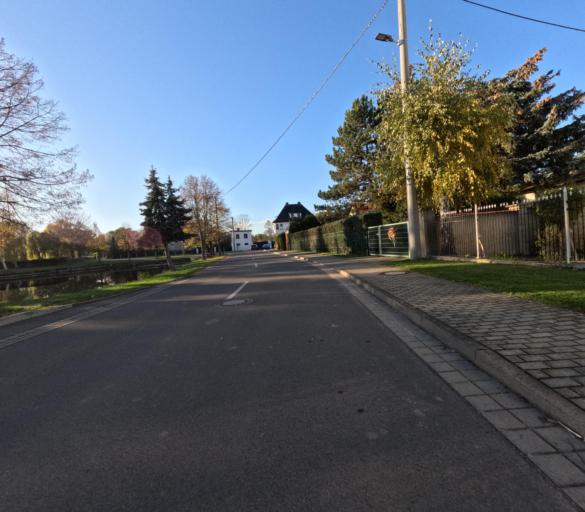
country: DE
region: Saxony-Anhalt
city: Zoschen
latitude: 51.3617
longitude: 12.1404
